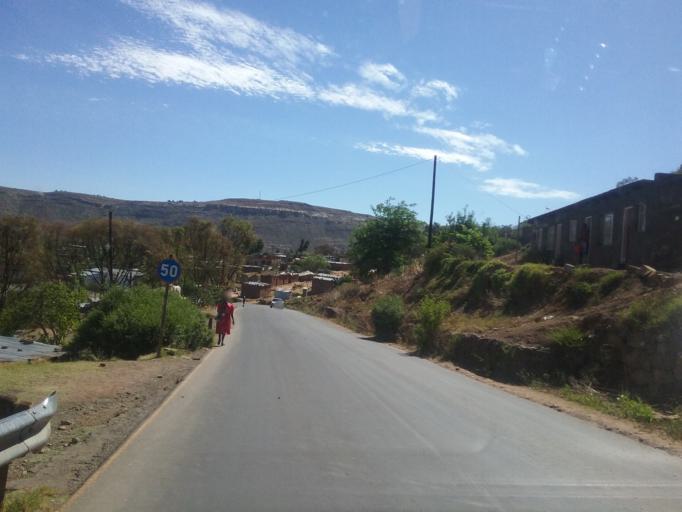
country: LS
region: Quthing
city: Quthing
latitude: -30.4019
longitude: 27.7038
